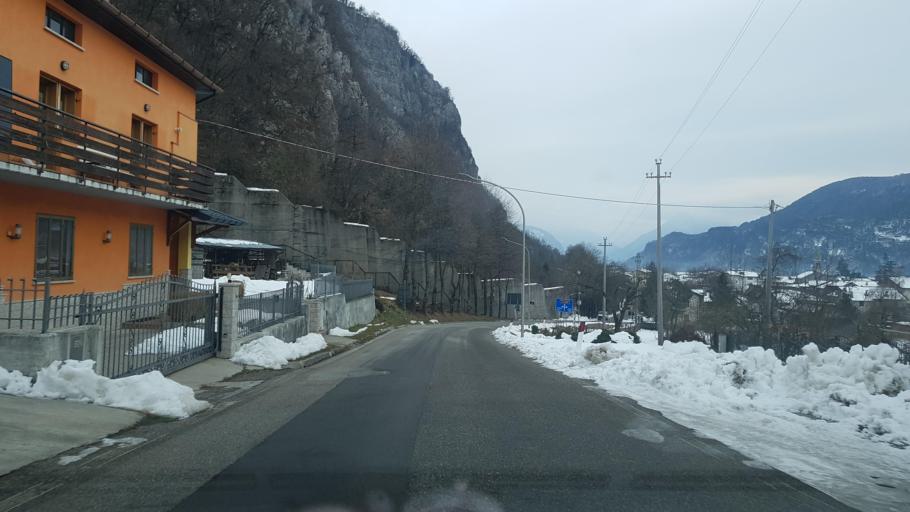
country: IT
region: Friuli Venezia Giulia
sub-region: Provincia di Udine
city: Villa Santina
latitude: 46.4185
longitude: 12.9189
